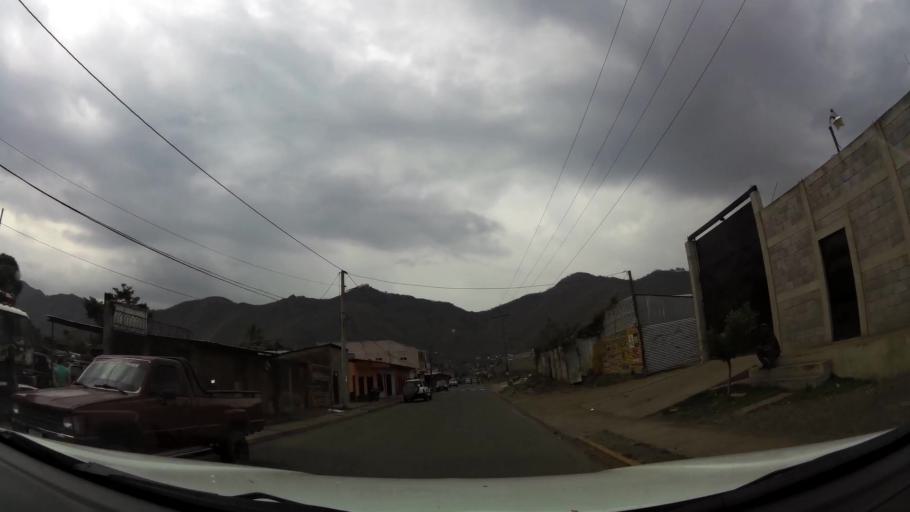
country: NI
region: Jinotega
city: Jinotega
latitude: 13.0977
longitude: -85.9987
